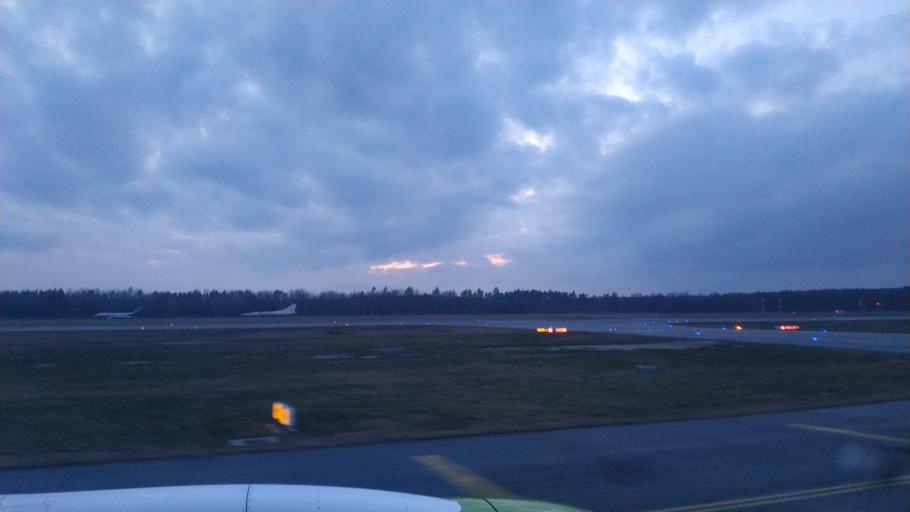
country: LV
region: Babite
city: Pinki
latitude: 56.9287
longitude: 23.9760
